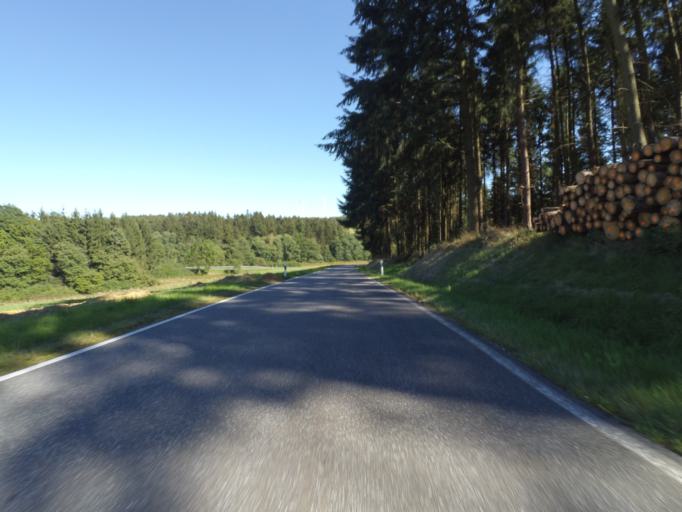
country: DE
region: Rheinland-Pfalz
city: Boxberg
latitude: 50.2687
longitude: 6.8837
